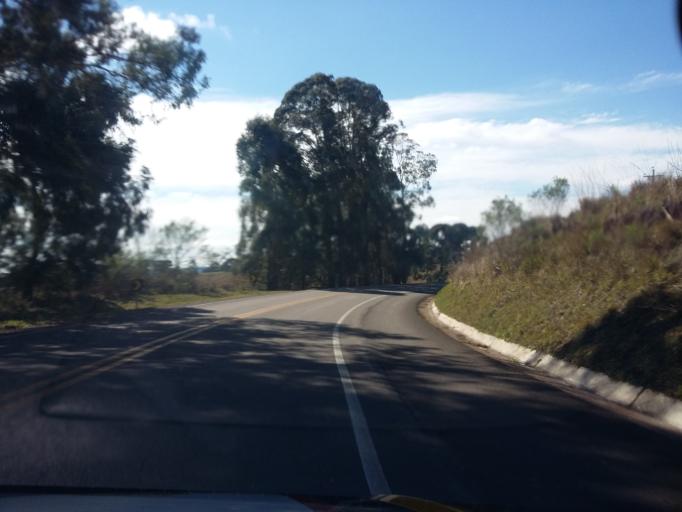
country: BR
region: Rio Grande do Sul
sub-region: Vacaria
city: Vacaria
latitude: -28.7146
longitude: -51.0876
